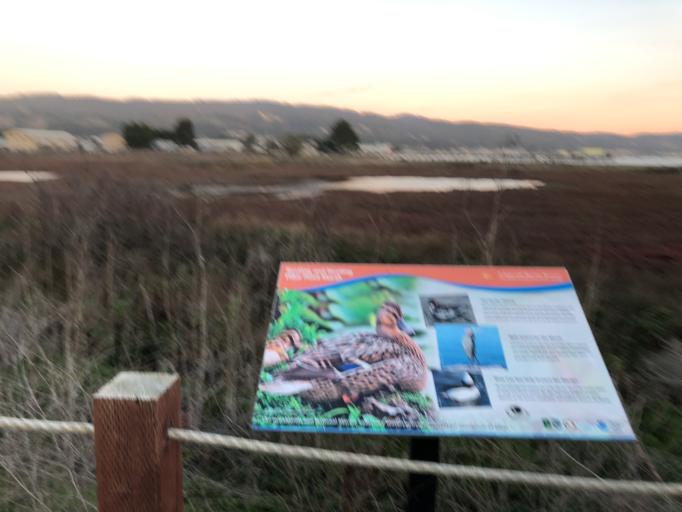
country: US
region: California
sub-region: San Mateo County
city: El Granada
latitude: 37.5012
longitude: -122.4966
